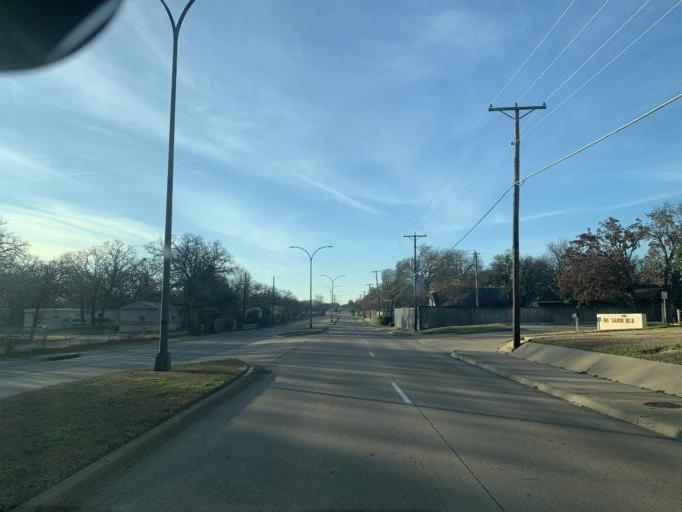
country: US
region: Texas
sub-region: Tarrant County
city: Arlington
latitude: 32.7716
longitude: -97.0737
